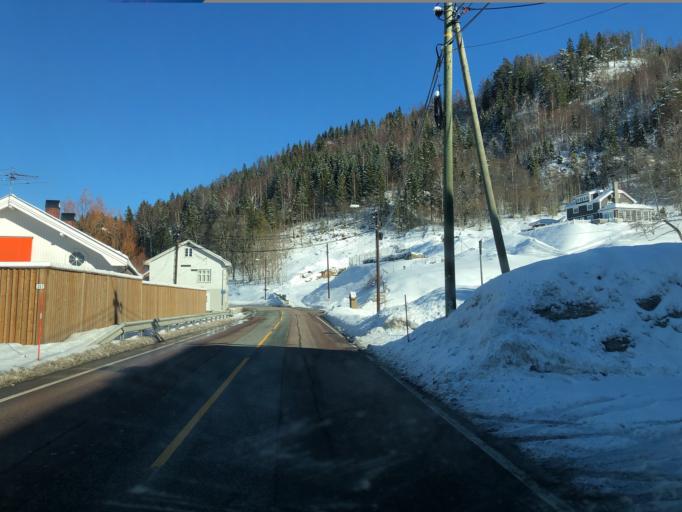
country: NO
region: Buskerud
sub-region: Lier
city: Tranby
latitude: 59.8397
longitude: 10.2635
